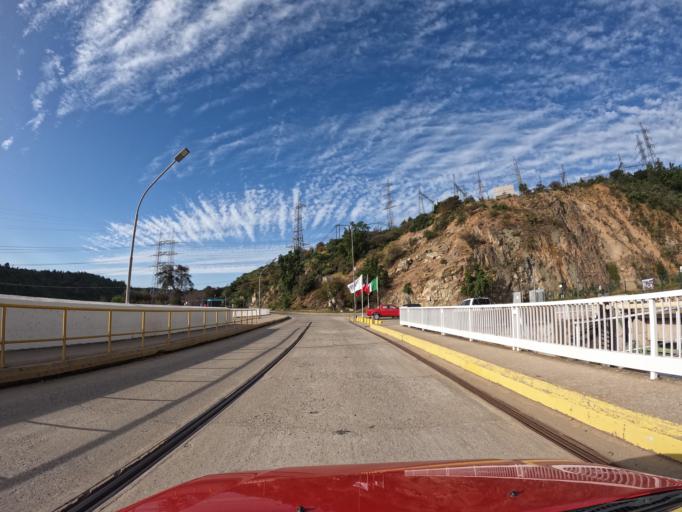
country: CL
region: Valparaiso
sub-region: San Antonio Province
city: San Antonio
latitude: -34.0410
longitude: -71.5878
